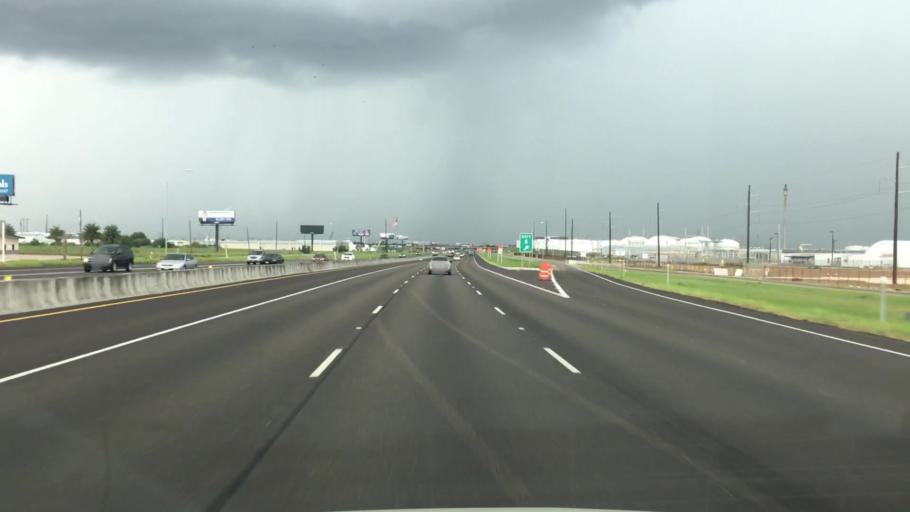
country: US
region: Texas
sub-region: Nueces County
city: Corpus Christi
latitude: 27.8073
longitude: -97.4932
